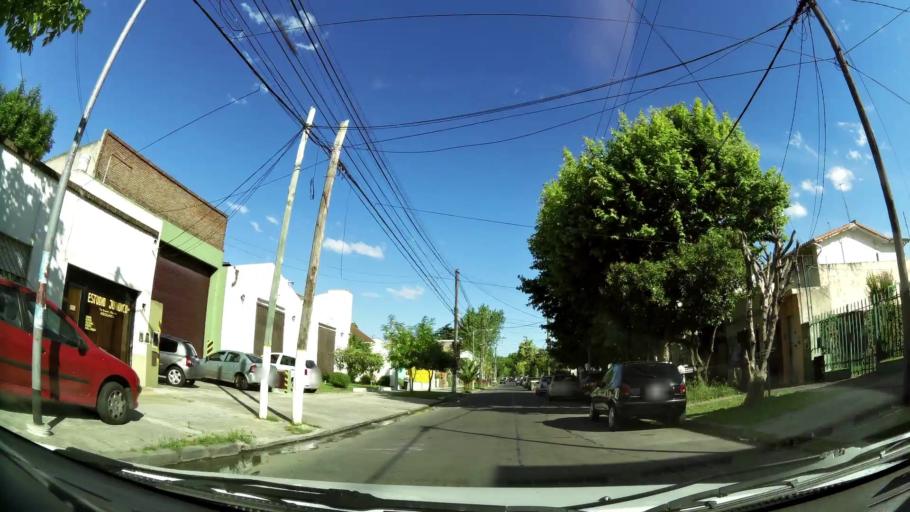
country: AR
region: Buenos Aires
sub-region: Partido de General San Martin
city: General San Martin
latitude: -34.5368
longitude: -58.5609
